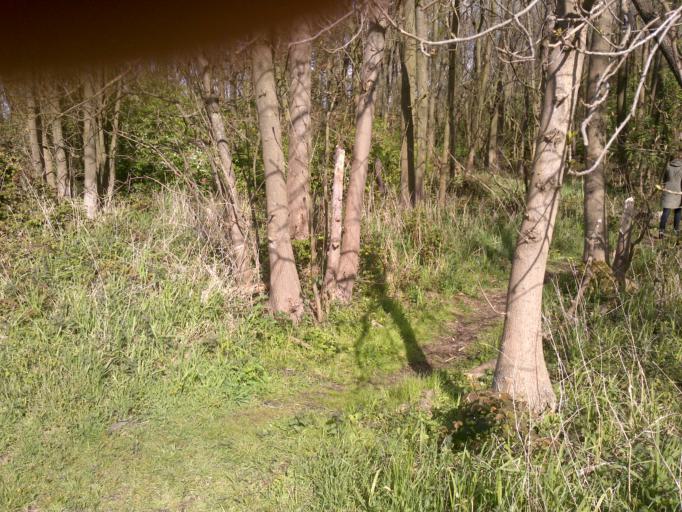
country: NL
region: South Holland
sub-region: Gemeente Noordwijkerhout
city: Noordwijkerhout
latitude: 52.2618
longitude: 4.5226
